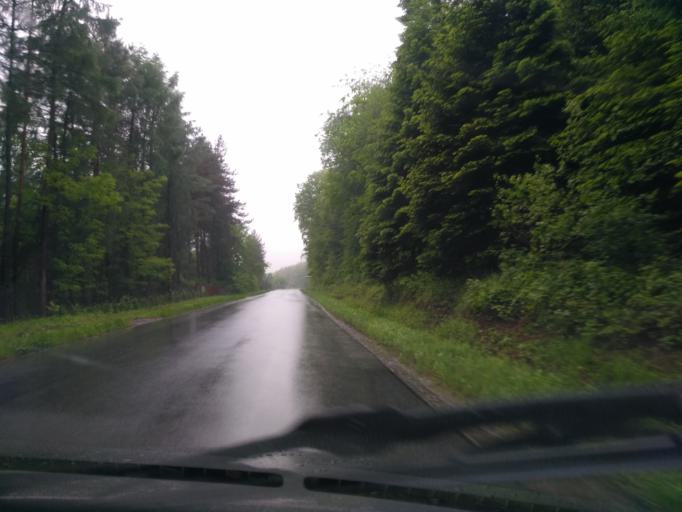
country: PL
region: Subcarpathian Voivodeship
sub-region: Powiat jasielski
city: Debowiec
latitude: 49.6593
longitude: 21.4255
